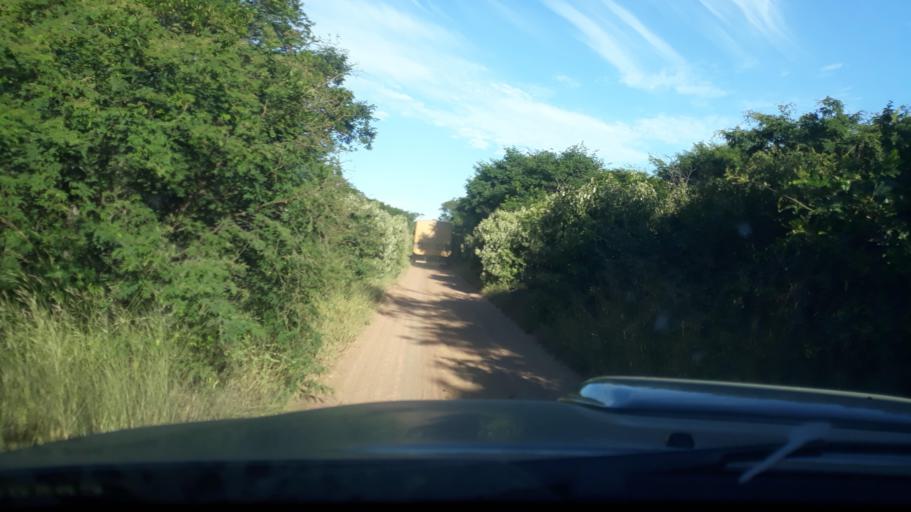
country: BR
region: Bahia
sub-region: Riacho De Santana
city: Riacho de Santana
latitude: -13.8575
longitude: -43.0426
